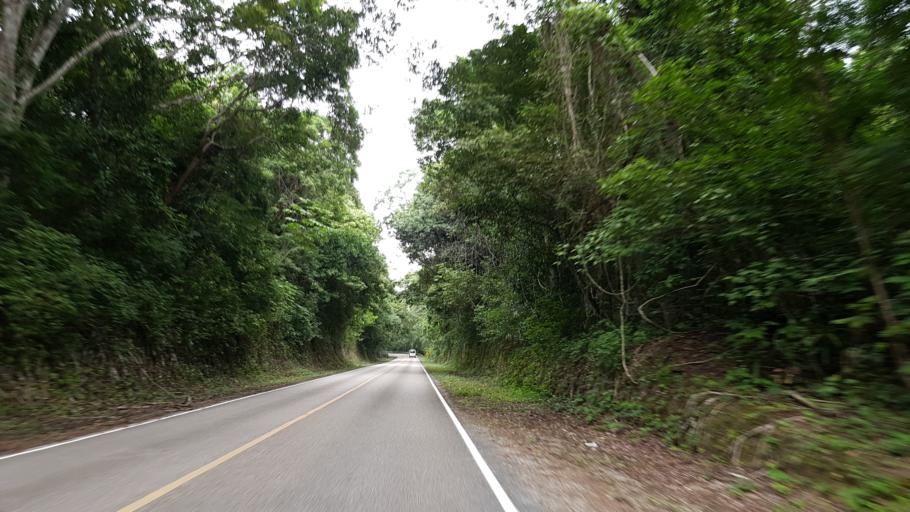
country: GT
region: Peten
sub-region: Municipio de San Jose
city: San Jose
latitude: 17.2123
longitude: -89.6140
